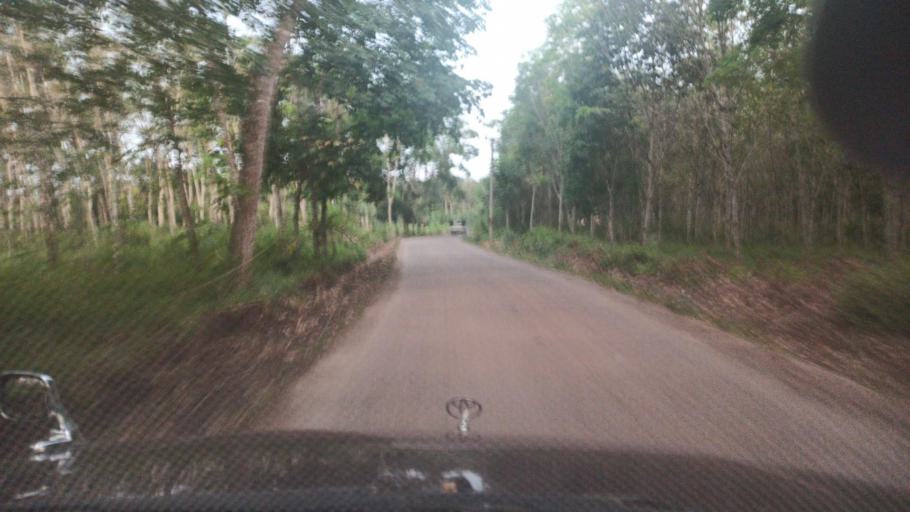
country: ID
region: South Sumatra
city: Gunungmenang
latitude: -3.2970
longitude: 104.1433
